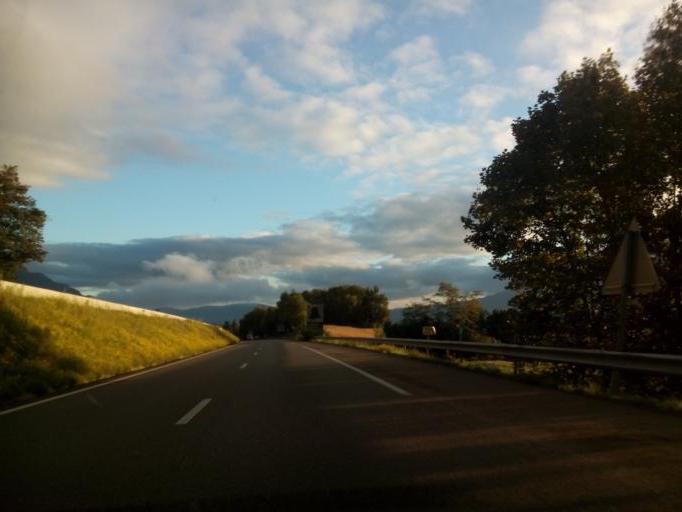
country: FR
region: Rhone-Alpes
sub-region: Departement de la Savoie
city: La Motte-Servolex
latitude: 45.5856
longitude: 5.8557
